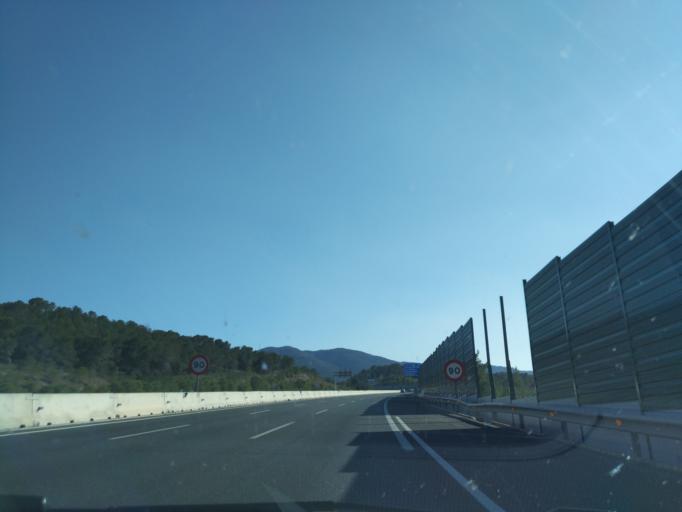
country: ES
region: Murcia
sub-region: Murcia
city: Murcia
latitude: 37.9306
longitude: -1.1549
